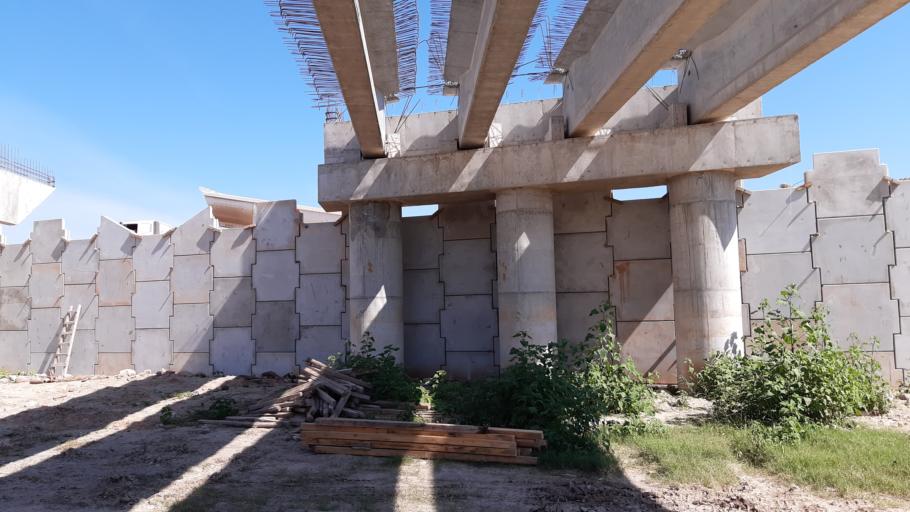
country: AR
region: Jujuy
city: La Mendieta
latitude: -24.3729
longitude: -64.9758
